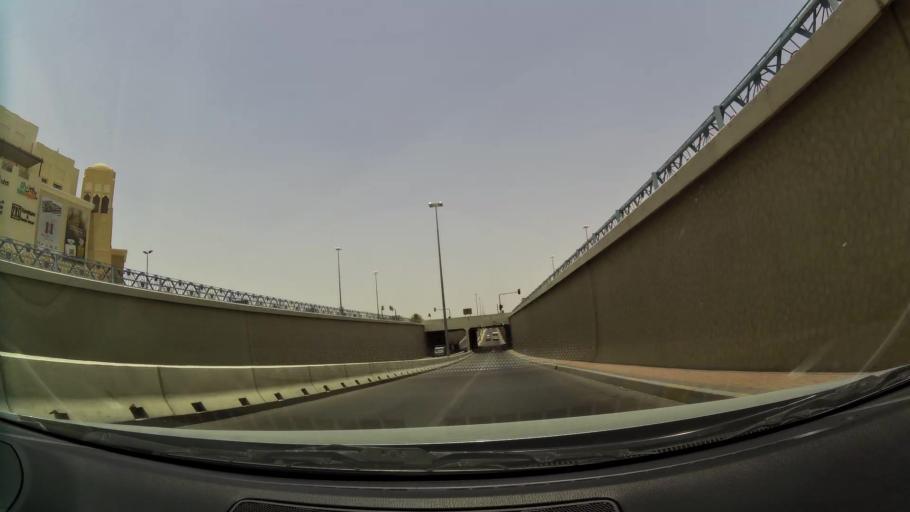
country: AE
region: Abu Dhabi
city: Al Ain
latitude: 24.2056
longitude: 55.7616
